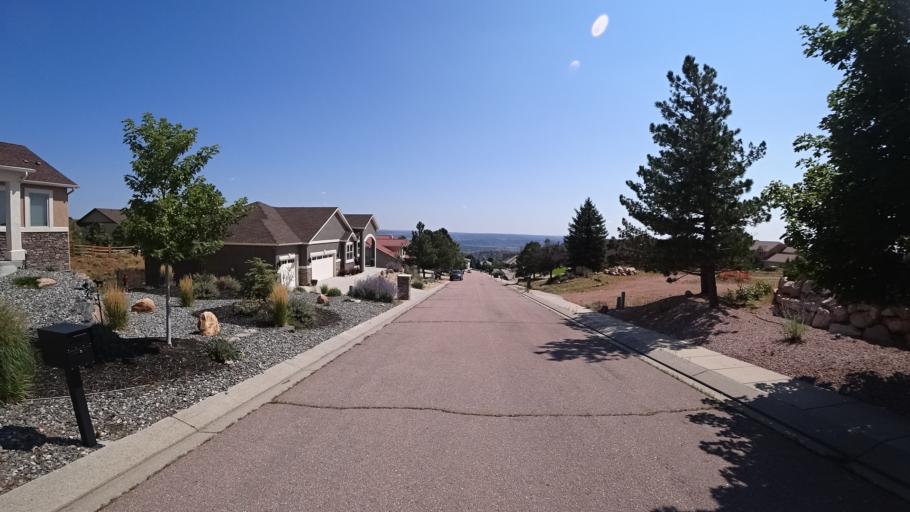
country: US
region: Colorado
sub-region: El Paso County
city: Manitou Springs
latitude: 38.9214
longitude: -104.8792
